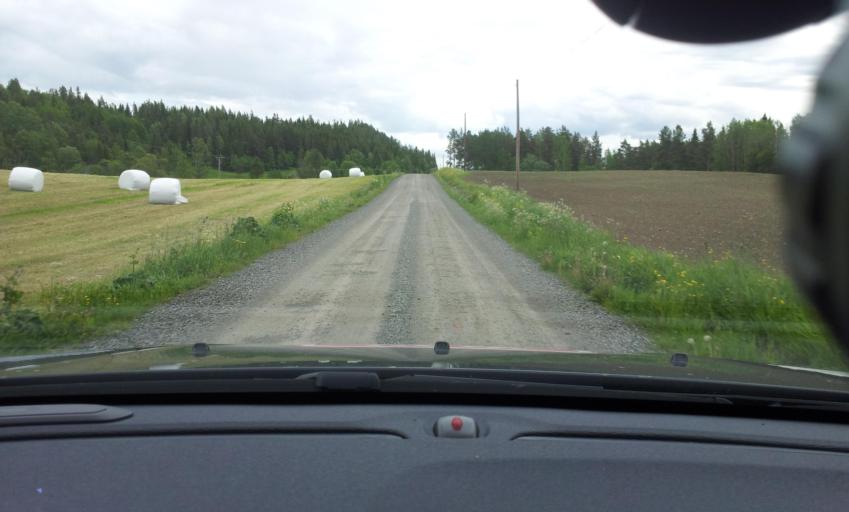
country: SE
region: Jaemtland
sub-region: OEstersunds Kommun
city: Brunflo
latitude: 62.9703
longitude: 14.6894
